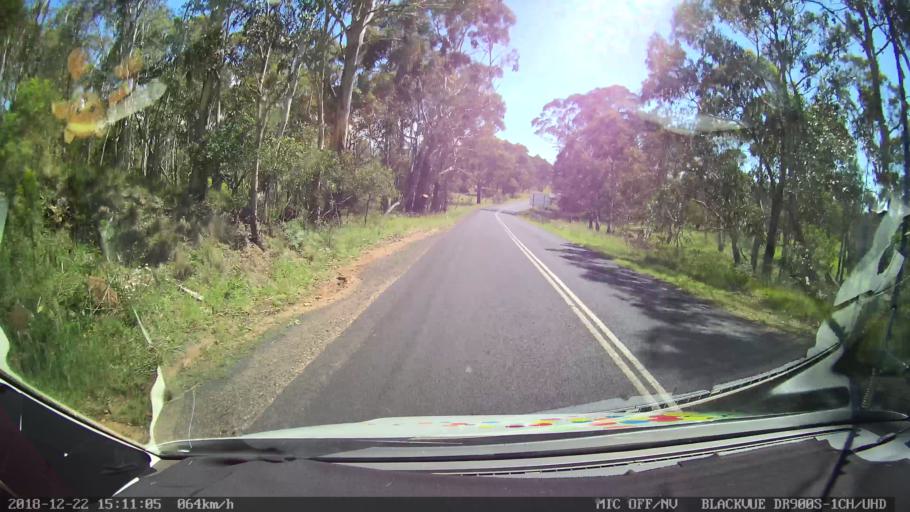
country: AU
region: New South Wales
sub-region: Bellingen
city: Dorrigo
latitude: -30.3413
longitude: 152.4052
